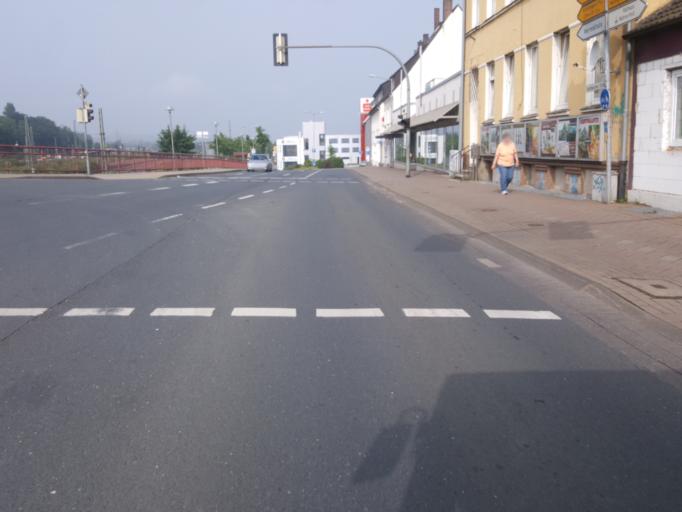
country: DE
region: North Rhine-Westphalia
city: Loehne
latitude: 52.1982
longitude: 8.7201
